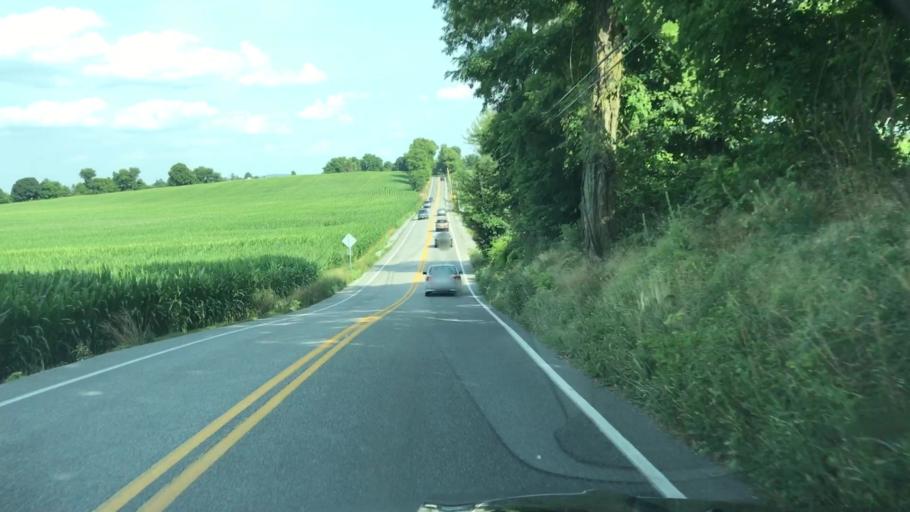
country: US
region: Pennsylvania
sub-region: York County
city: Dillsburg
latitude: 40.1682
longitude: -77.0496
